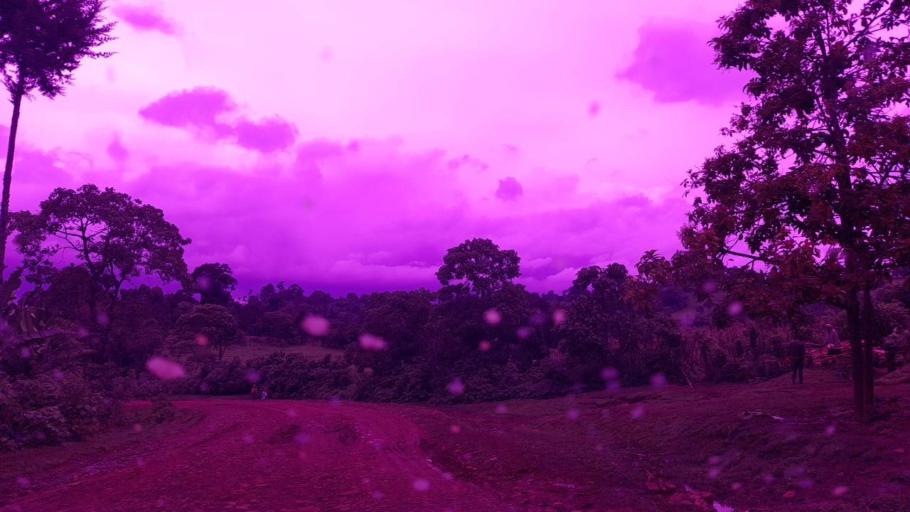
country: ET
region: Southern Nations, Nationalities, and People's Region
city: Tippi
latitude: 7.5778
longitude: 35.6643
